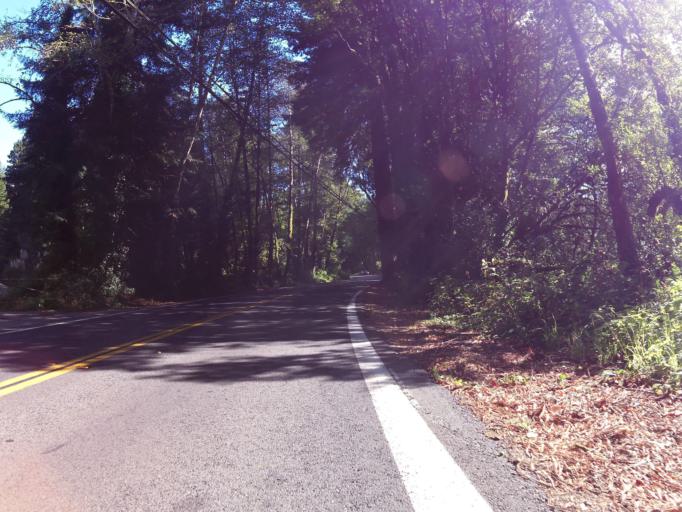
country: US
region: California
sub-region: Del Norte County
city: Bertsch-Oceanview
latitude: 41.8508
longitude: -124.1204
